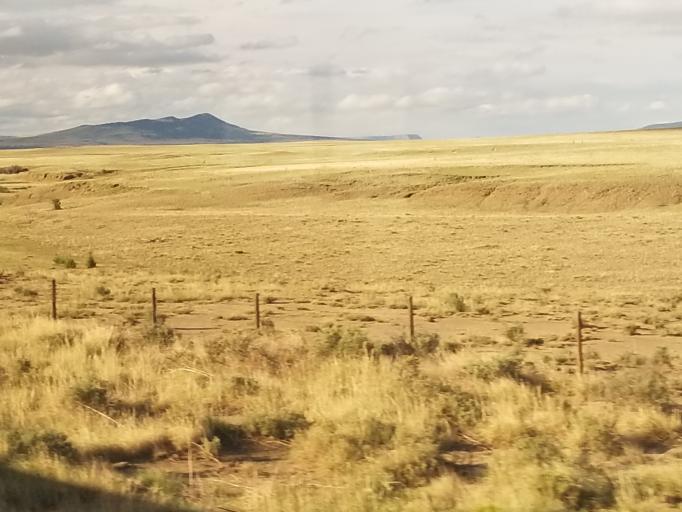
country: US
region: New Mexico
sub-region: Colfax County
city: Springer
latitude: 36.4976
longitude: -104.5451
